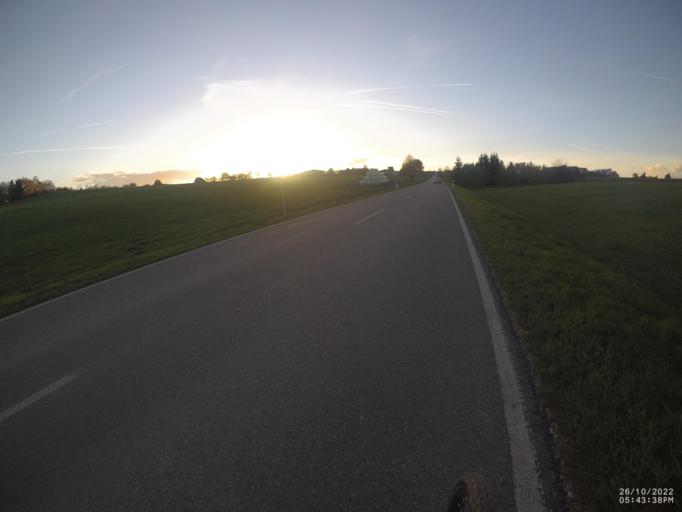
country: DE
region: Baden-Wuerttemberg
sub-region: Regierungsbezirk Stuttgart
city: Hohenstadt
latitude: 48.5430
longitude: 9.6743
